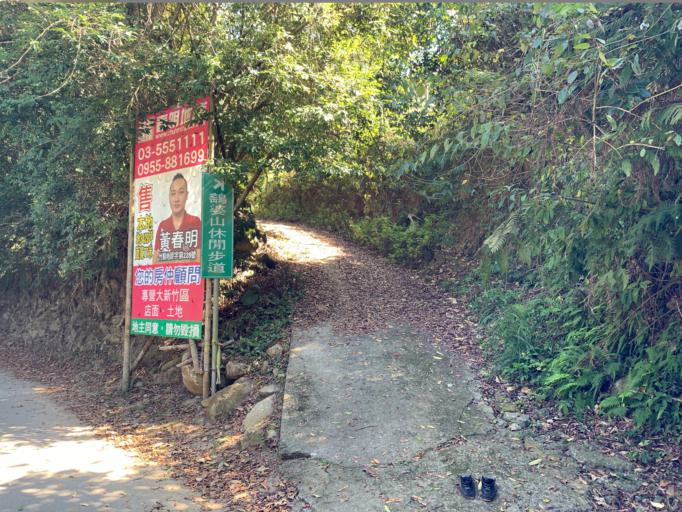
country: TW
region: Taiwan
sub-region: Miaoli
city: Miaoli
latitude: 24.4464
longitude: 120.9048
